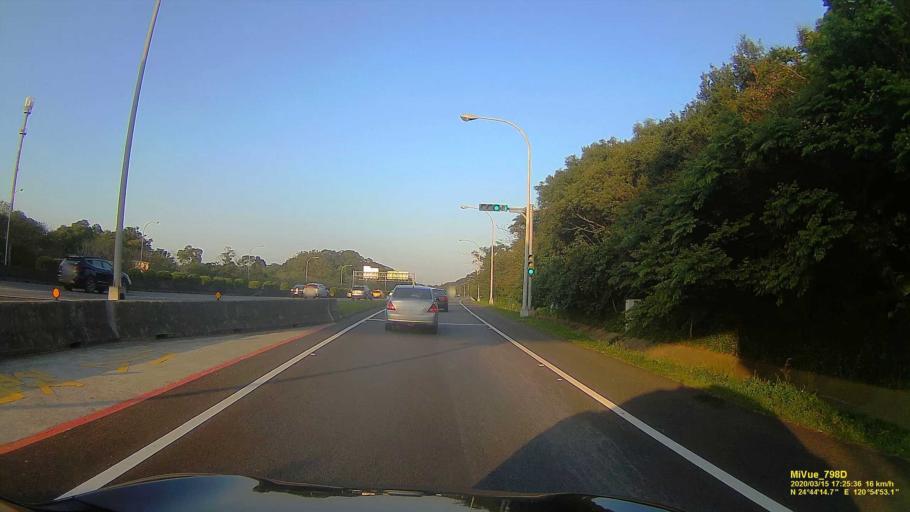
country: TW
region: Taiwan
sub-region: Hsinchu
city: Hsinchu
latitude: 24.7375
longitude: 120.9149
